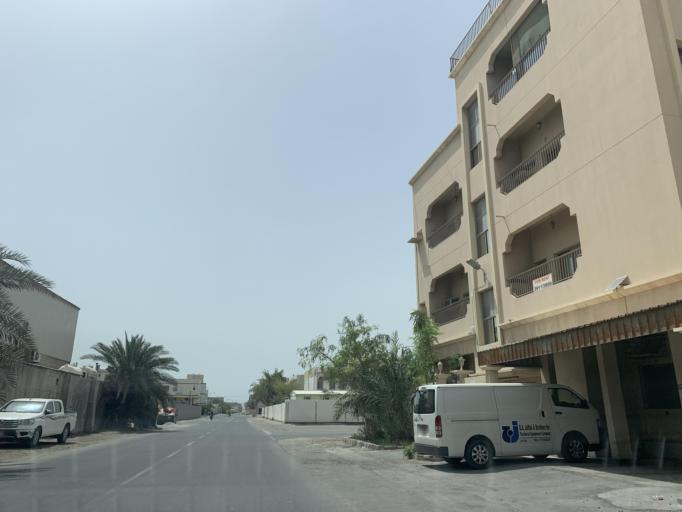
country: BH
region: Northern
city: Sitrah
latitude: 26.1397
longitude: 50.6017
